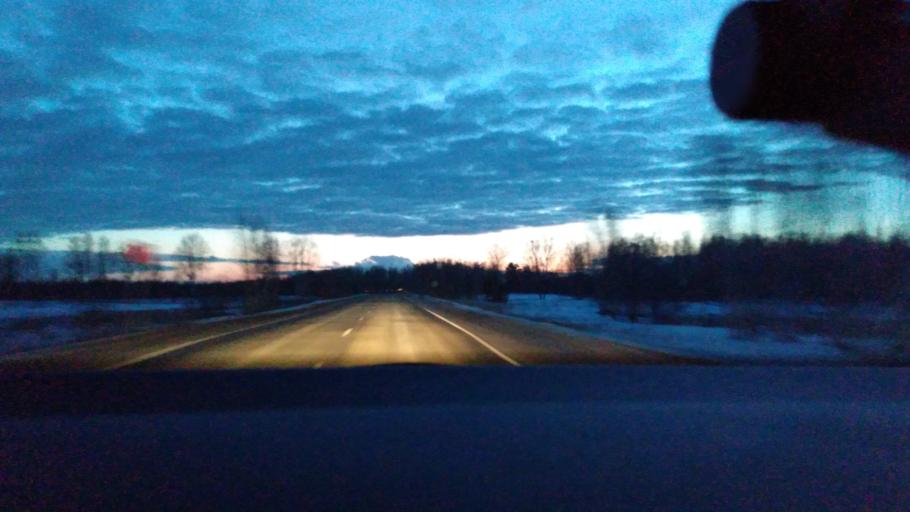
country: RU
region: Moskovskaya
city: Krasnaya Poyma
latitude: 55.1425
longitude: 39.2131
